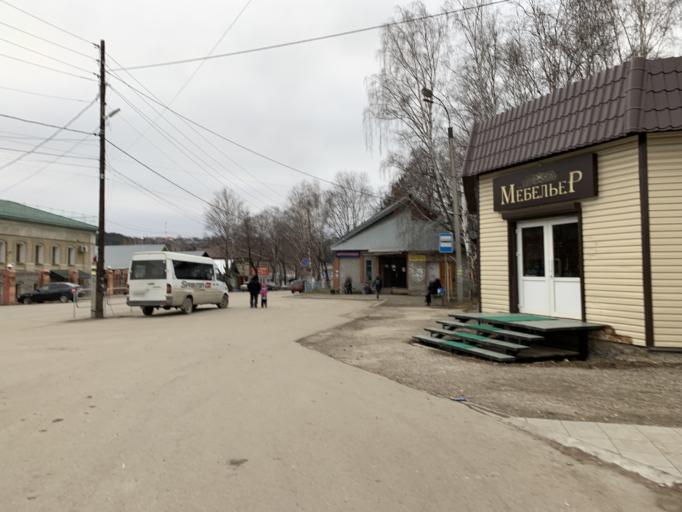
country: RU
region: Chelyabinsk
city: Nyazepetrovsk
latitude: 56.0528
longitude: 59.5946
